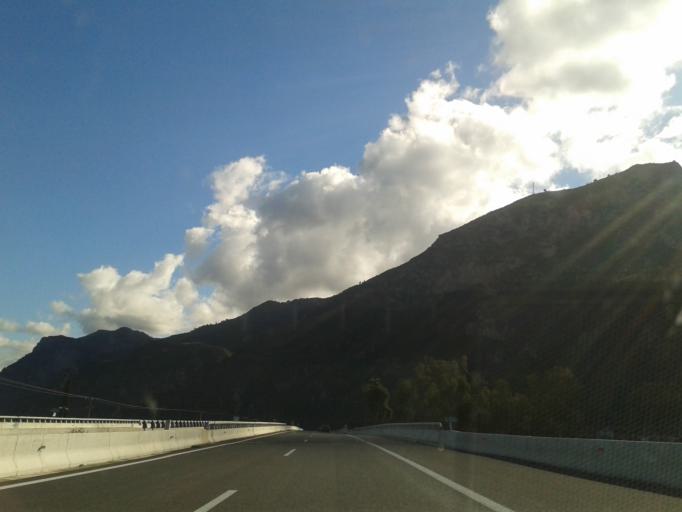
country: GR
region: West Greece
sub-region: Nomos Achaias
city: Temeni
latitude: 38.1966
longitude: 22.1520
